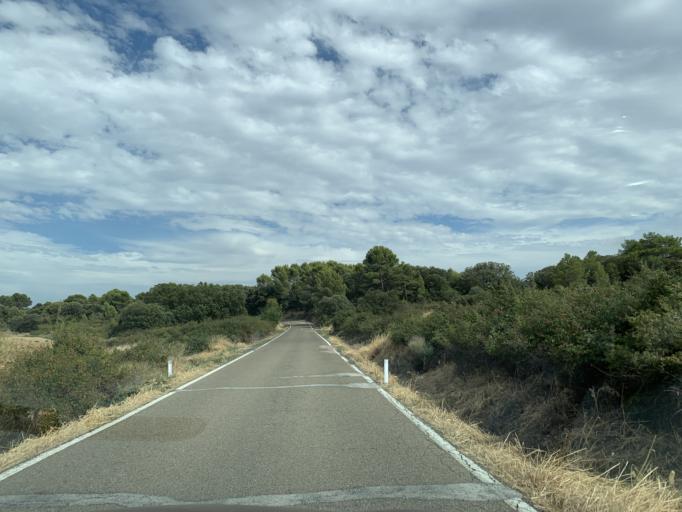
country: ES
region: Aragon
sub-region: Provincia de Zaragoza
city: Santa Eulalia de Gallego
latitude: 42.3157
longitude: -0.7432
